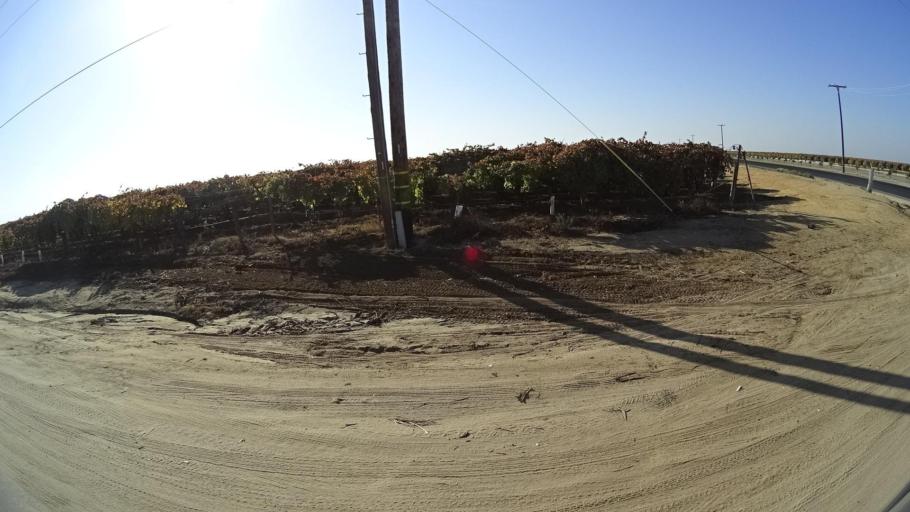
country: US
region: California
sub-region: Tulare County
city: Richgrove
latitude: 35.7325
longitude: -119.1504
